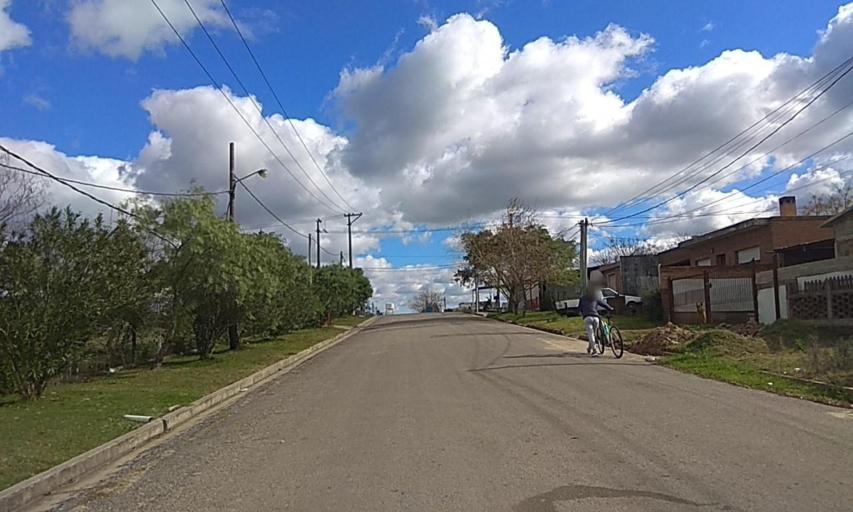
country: UY
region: Florida
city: Florida
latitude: -34.0880
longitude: -56.2321
